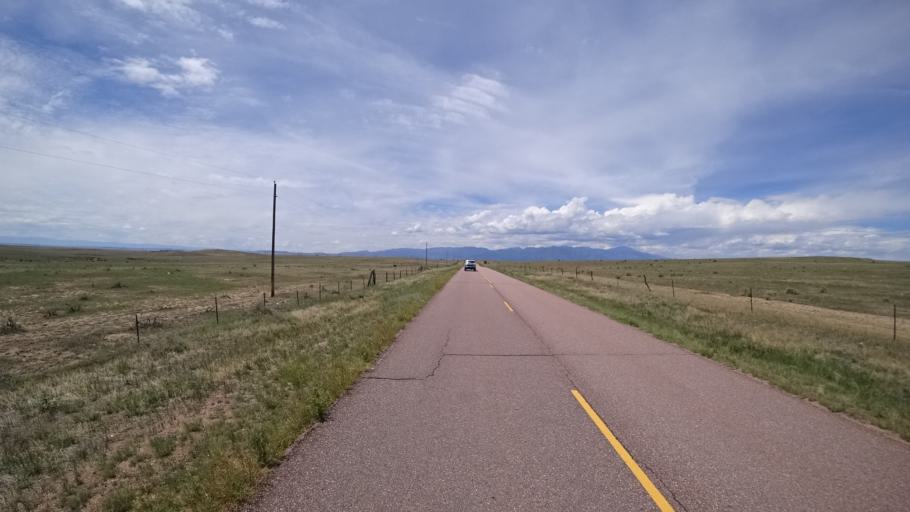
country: US
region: Colorado
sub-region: El Paso County
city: Fountain
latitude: 38.6940
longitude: -104.6047
